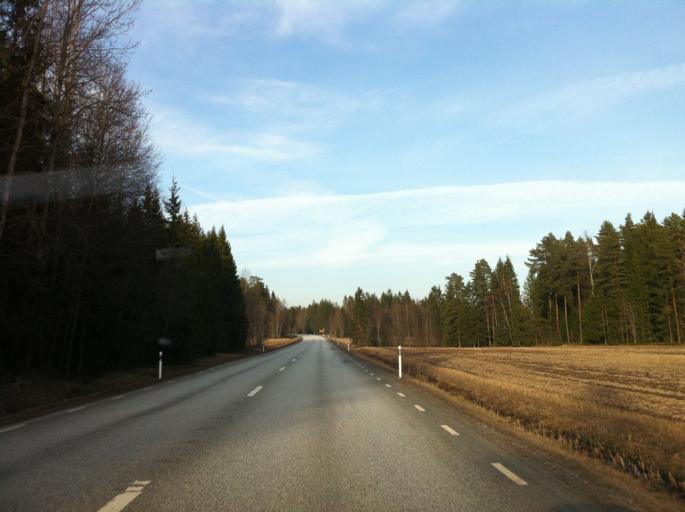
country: SE
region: Vaermland
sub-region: Storfors Kommun
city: Storfors
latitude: 59.4585
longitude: 14.2499
